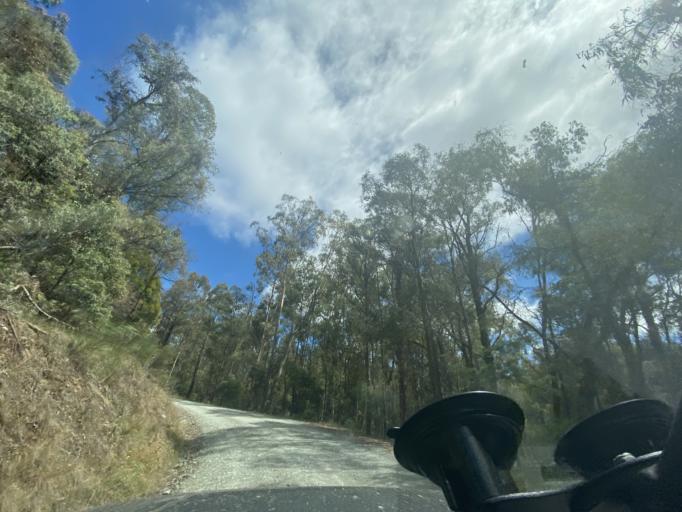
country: AU
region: Victoria
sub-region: Yarra Ranges
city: Millgrove
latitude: -37.5229
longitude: 146.0501
